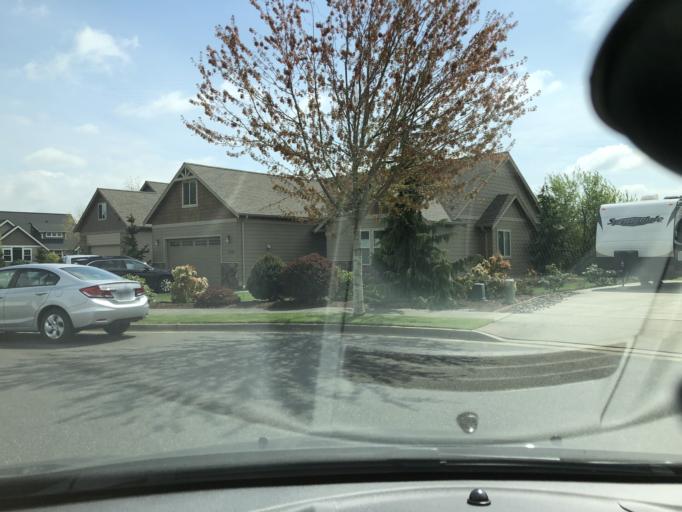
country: US
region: Washington
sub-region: Whatcom County
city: Lynden
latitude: 48.9565
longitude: -122.4240
